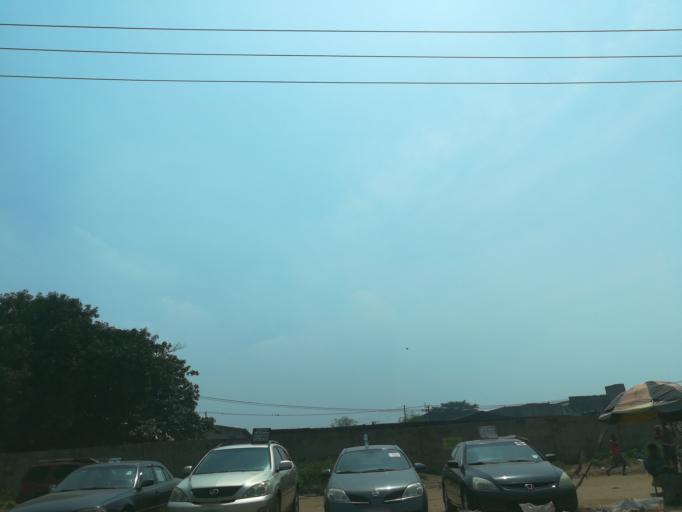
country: NG
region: Lagos
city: Ikorodu
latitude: 6.6322
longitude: 3.4830
